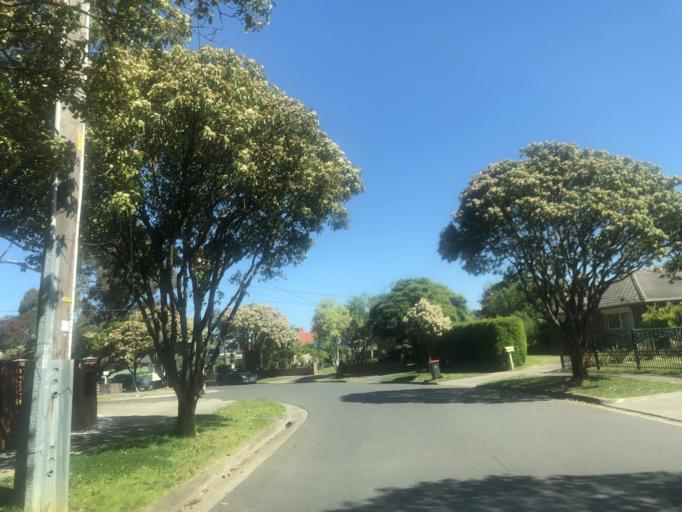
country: AU
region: Victoria
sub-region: Monash
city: Mulgrave
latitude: -37.9024
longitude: 145.1752
